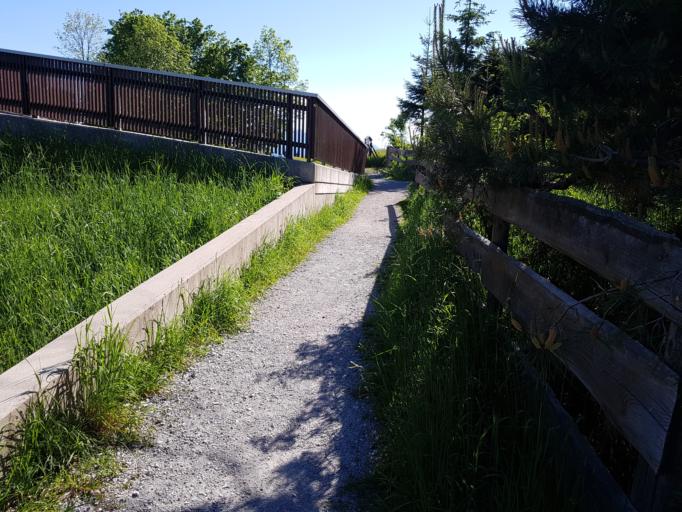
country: AT
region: Salzburg
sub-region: Politischer Bezirk Salzburg-Umgebung
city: Koppl
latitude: 47.7959
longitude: 13.1141
